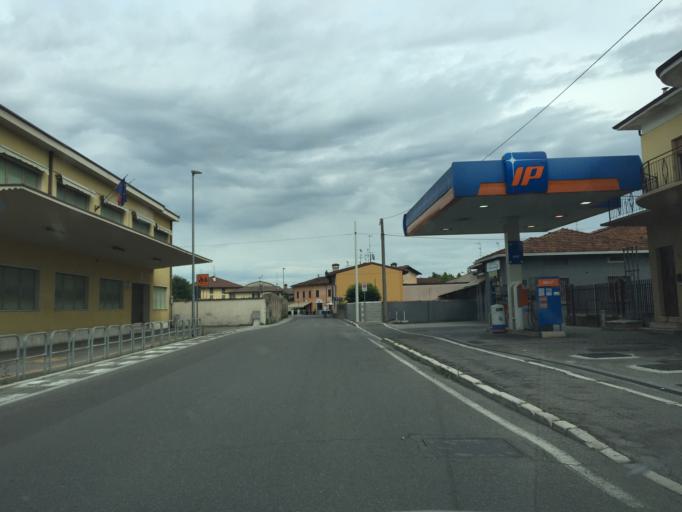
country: IT
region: Lombardy
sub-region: Provincia di Brescia
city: Ghedi
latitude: 45.4005
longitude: 10.2716
